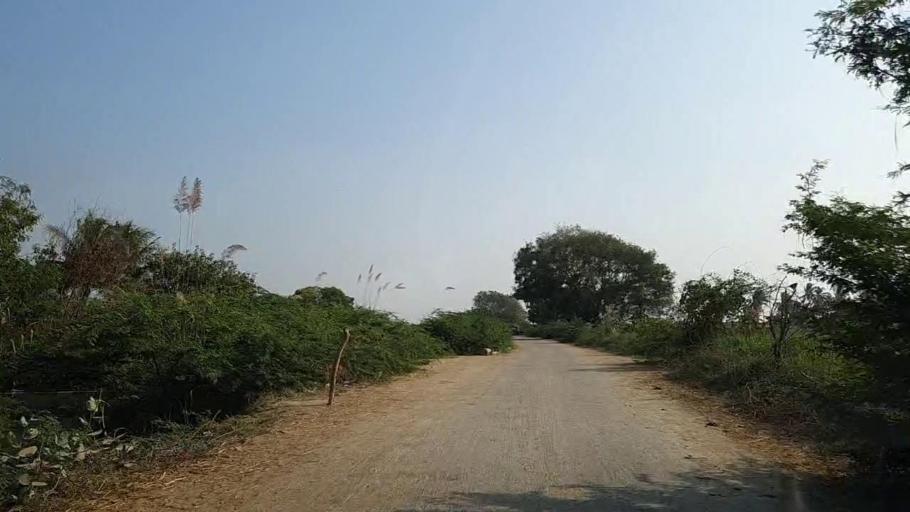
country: PK
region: Sindh
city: Mirpur Sakro
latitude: 24.6279
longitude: 67.6530
